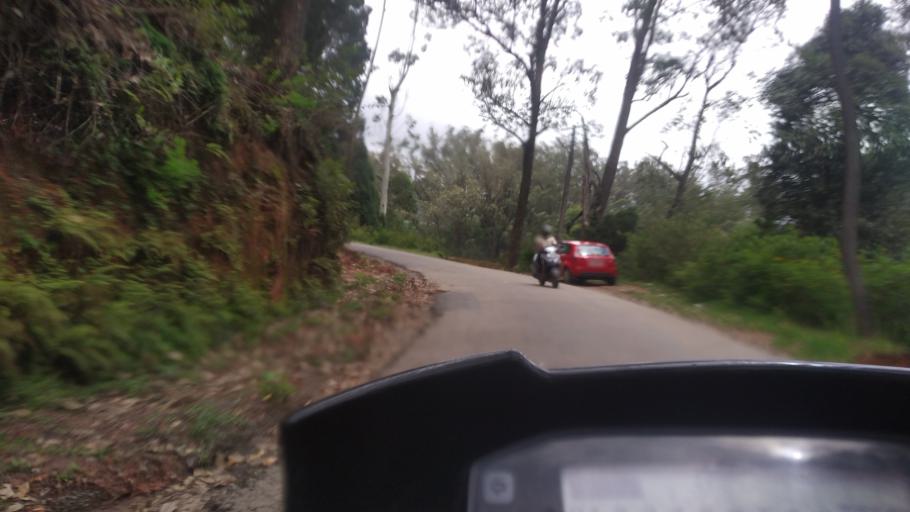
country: IN
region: Kerala
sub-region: Idukki
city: Munnar
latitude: 10.0647
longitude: 77.1037
